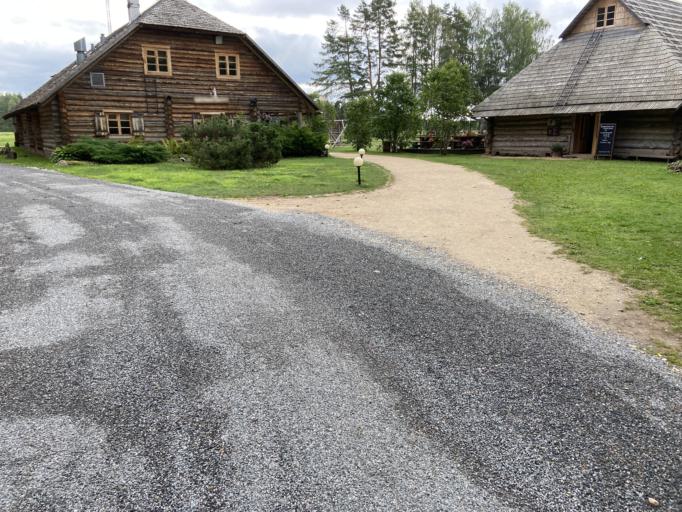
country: RU
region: Pskov
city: Pechory
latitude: 57.9432
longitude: 27.6500
